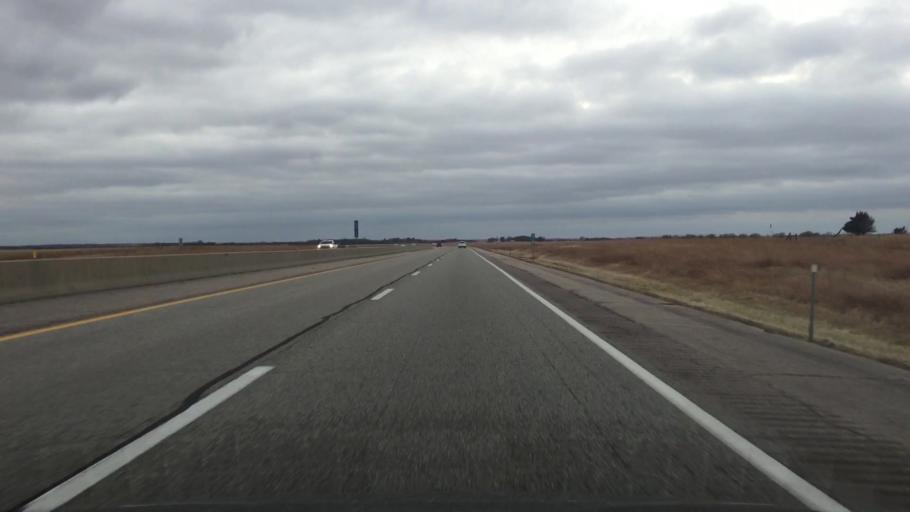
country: US
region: Kansas
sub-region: Butler County
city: El Dorado
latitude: 37.9045
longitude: -96.8246
